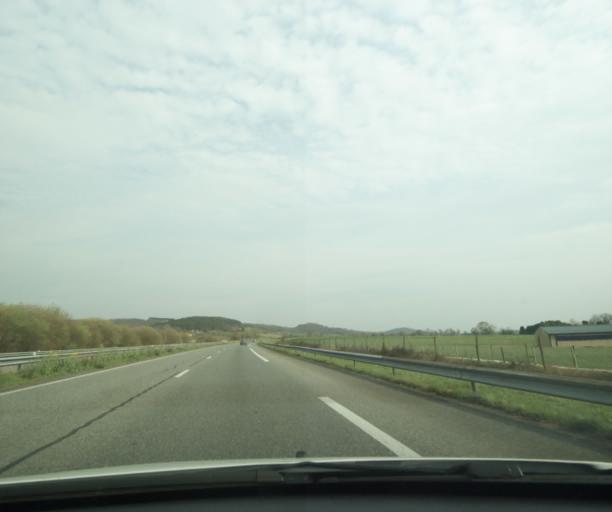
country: FR
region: Aquitaine
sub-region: Departement des Pyrenees-Atlantiques
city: Denguin
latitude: 43.3850
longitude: -0.5155
